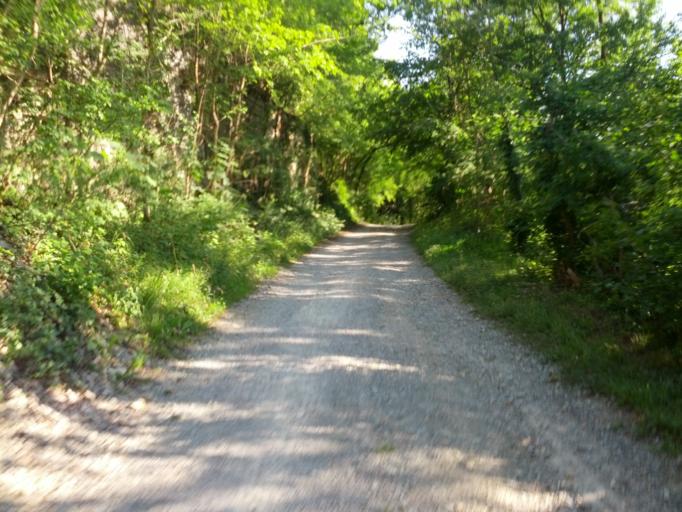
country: DE
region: Thuringia
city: Creuzburg
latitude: 51.0508
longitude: 10.2530
